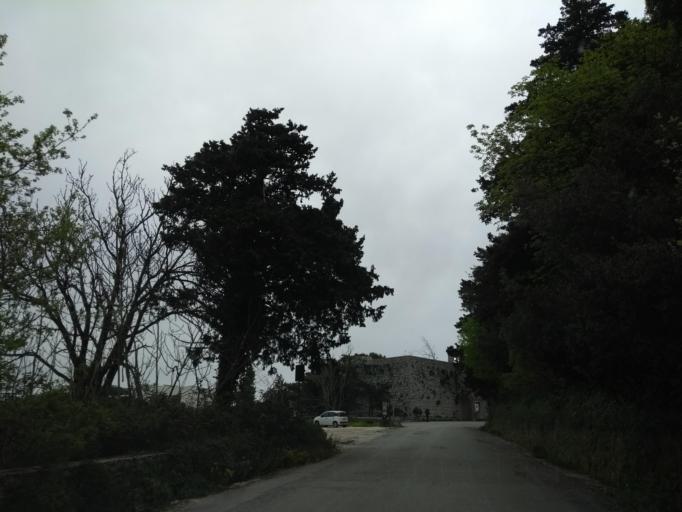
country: IT
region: Sicily
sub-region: Trapani
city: Erice
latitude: 38.0414
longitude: 12.5871
